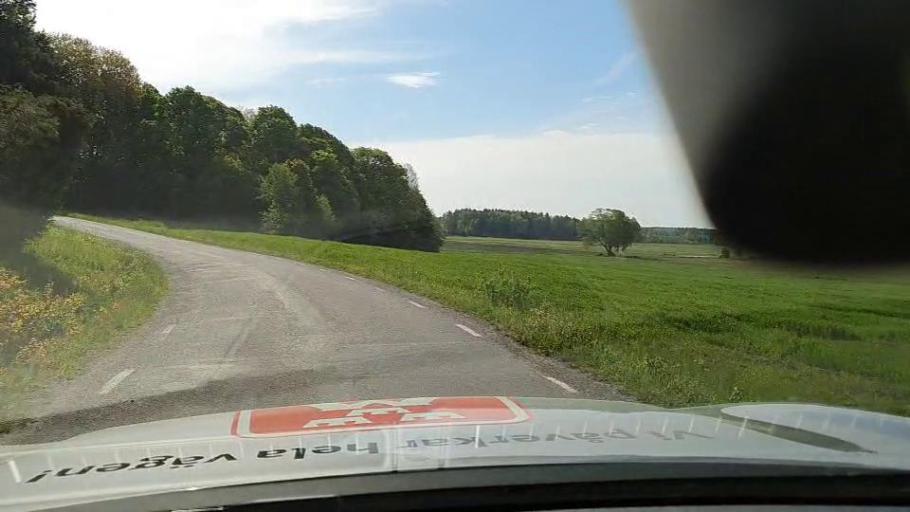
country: SE
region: Soedermanland
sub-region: Eskilstuna Kommun
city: Arla
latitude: 59.2572
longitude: 16.6954
